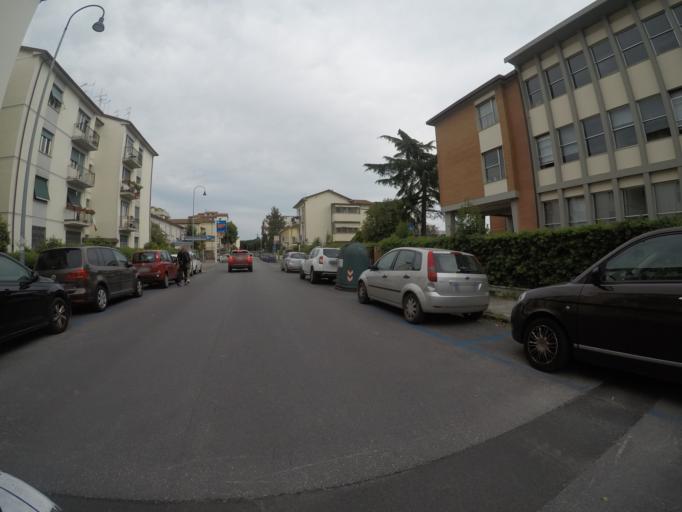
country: IT
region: Tuscany
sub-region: Province of Pisa
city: Pisa
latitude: 43.7214
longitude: 10.4099
